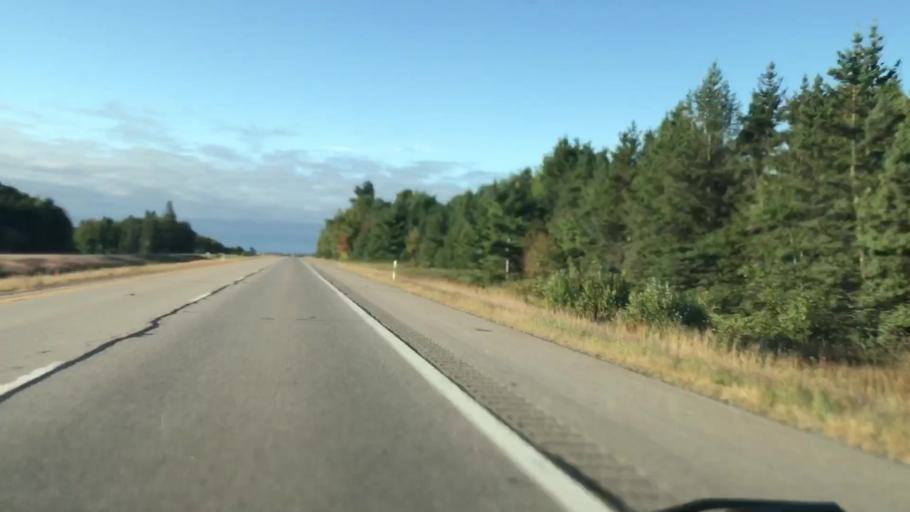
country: US
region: Michigan
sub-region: Chippewa County
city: Sault Ste. Marie
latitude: 46.4288
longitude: -84.3917
